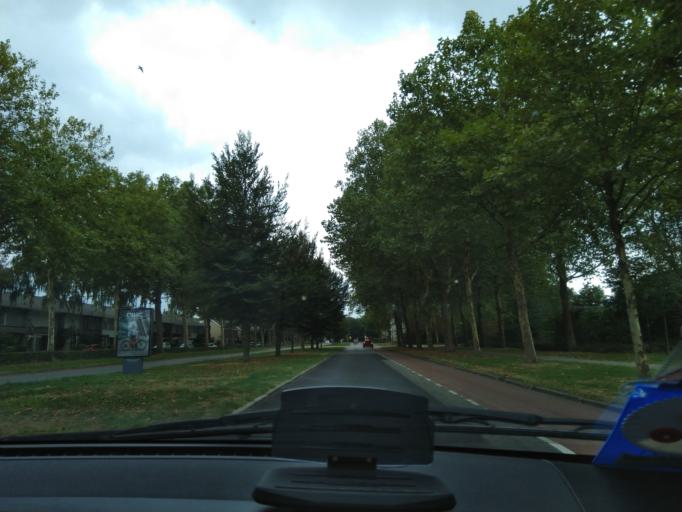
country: NL
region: North Brabant
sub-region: Gemeente Oosterhout
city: Oosterhout
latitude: 51.6238
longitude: 4.8529
